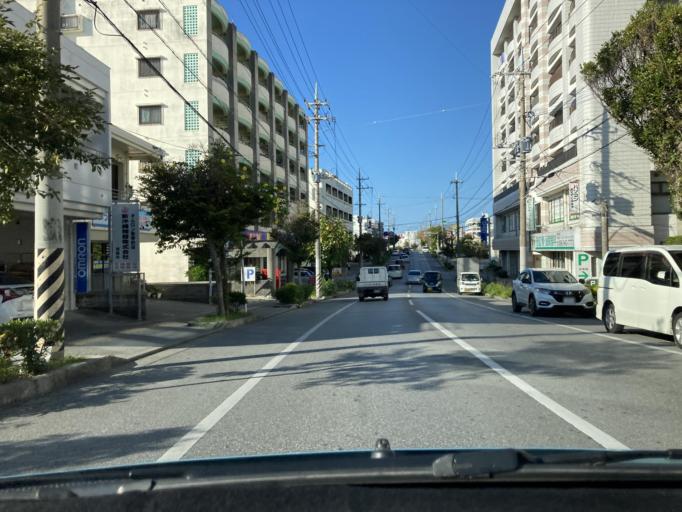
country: JP
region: Okinawa
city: Ginowan
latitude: 26.2521
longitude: 127.7139
